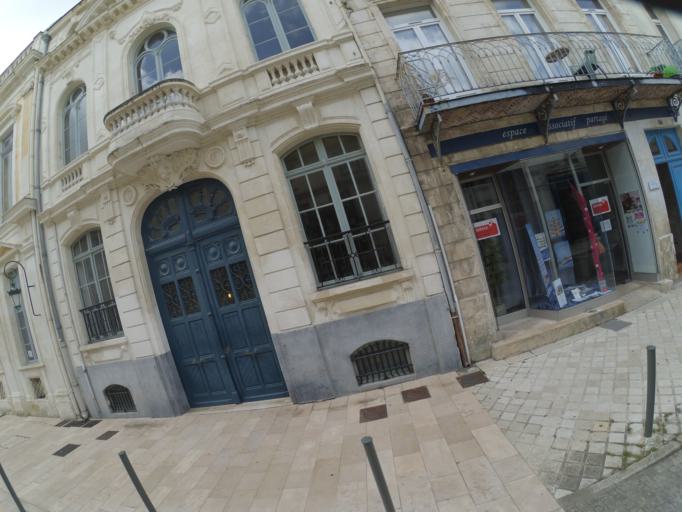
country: FR
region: Poitou-Charentes
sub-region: Departement de la Charente-Maritime
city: Rochefort
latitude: 45.9380
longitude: -0.9607
